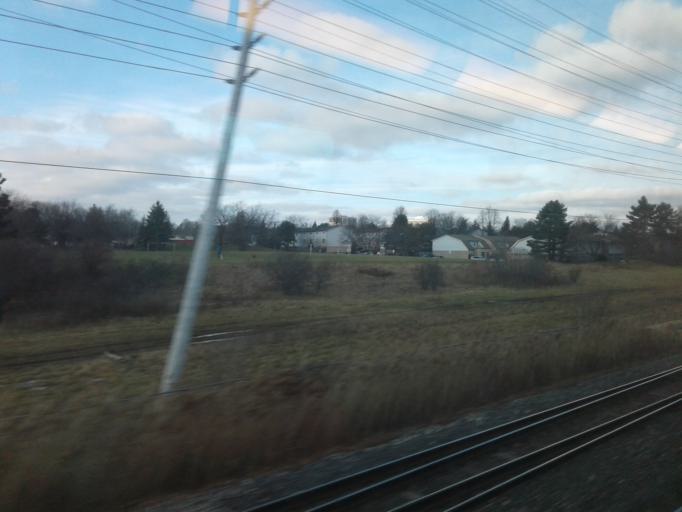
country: CA
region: Ontario
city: Oakville
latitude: 43.5034
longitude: -79.6434
